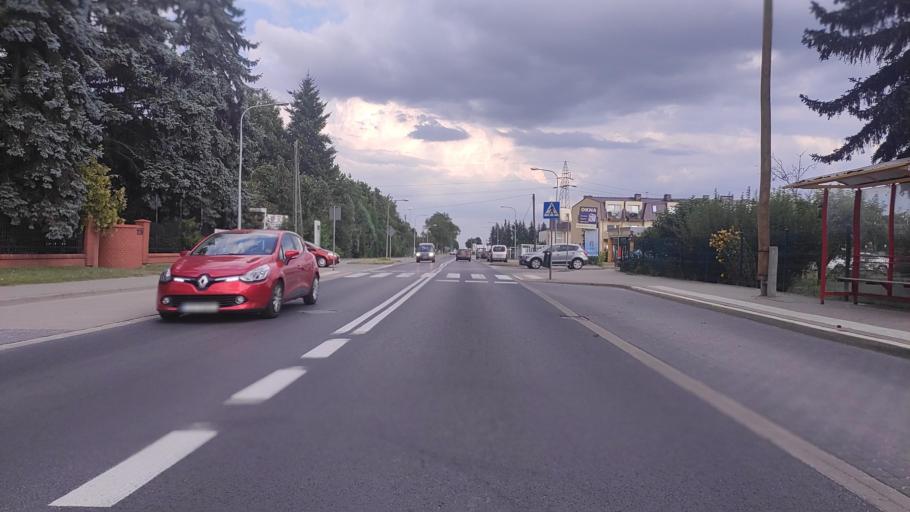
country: PL
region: Greater Poland Voivodeship
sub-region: Powiat poznanski
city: Swarzedz
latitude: 52.4077
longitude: 17.0984
